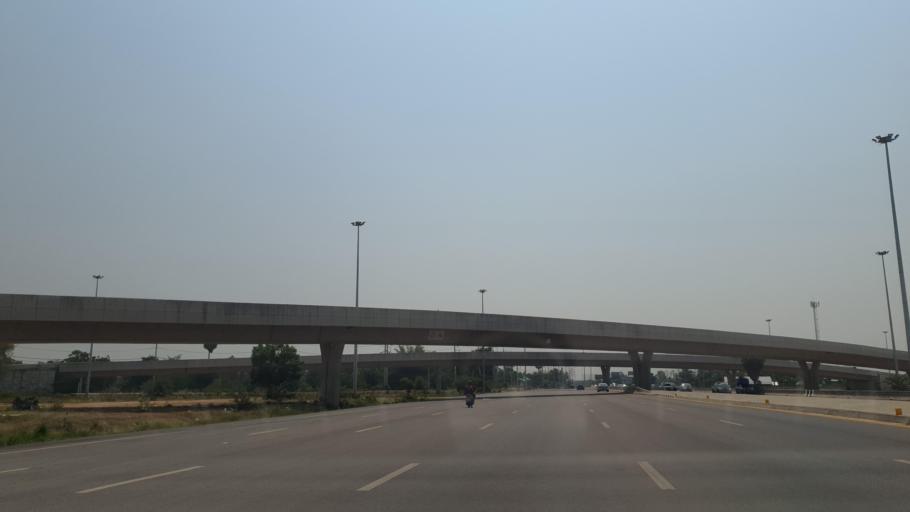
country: TH
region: Kanchanaburi
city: Kanchanaburi
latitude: 14.0437
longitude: 99.6021
